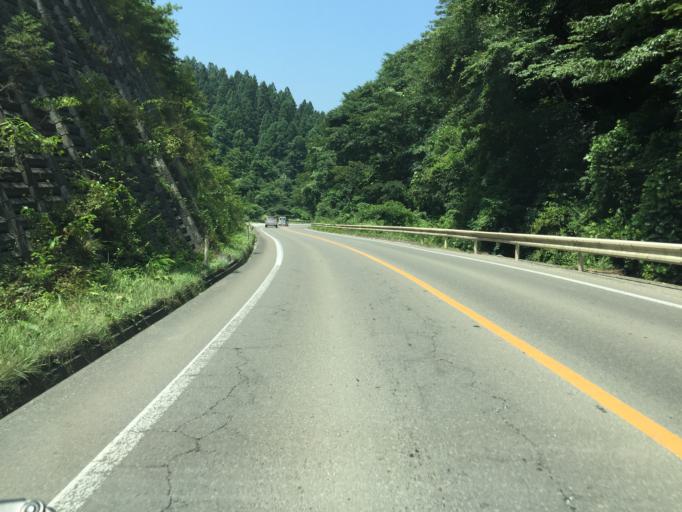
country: JP
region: Miyagi
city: Marumori
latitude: 37.8548
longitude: 140.8513
